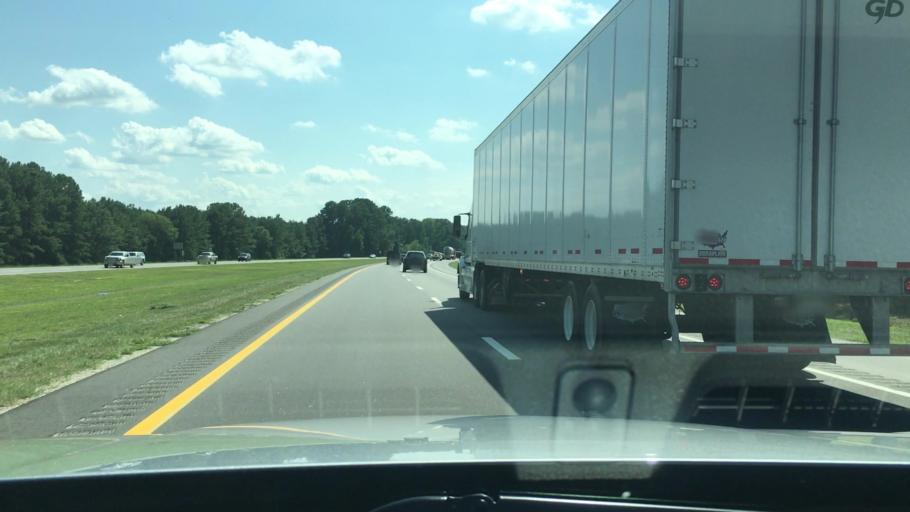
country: US
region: North Carolina
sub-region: Cumberland County
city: Vander
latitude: 34.9868
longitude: -78.8408
